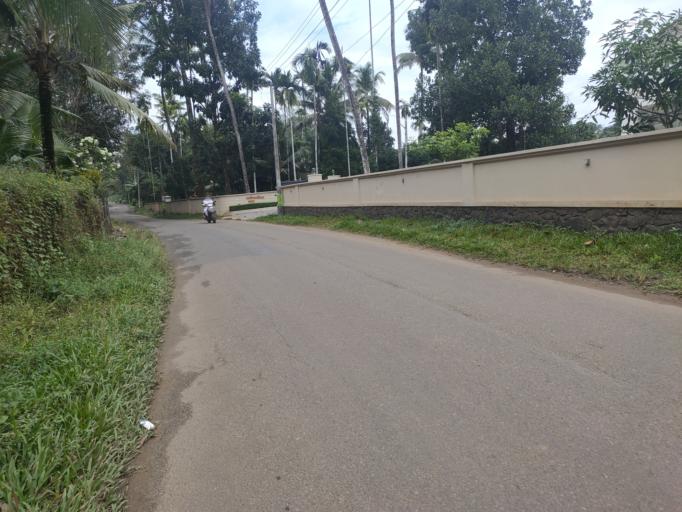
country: IN
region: Kerala
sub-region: Ernakulam
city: Muvattupula
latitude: 9.9924
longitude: 76.6370
